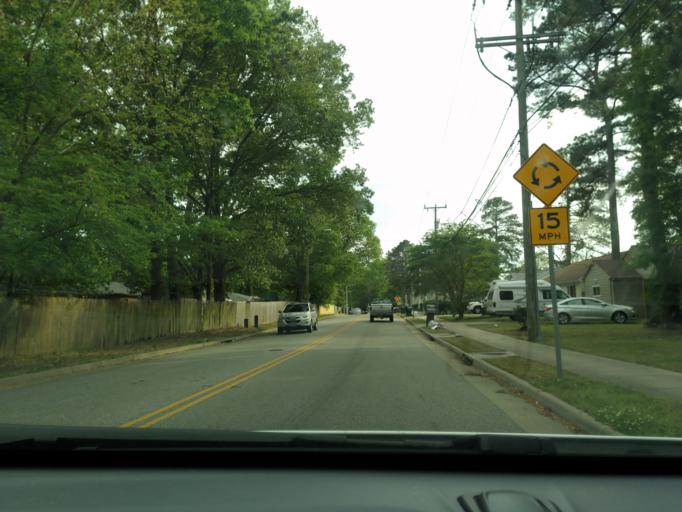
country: US
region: Virginia
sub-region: York County
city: Yorktown
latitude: 37.1615
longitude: -76.5257
